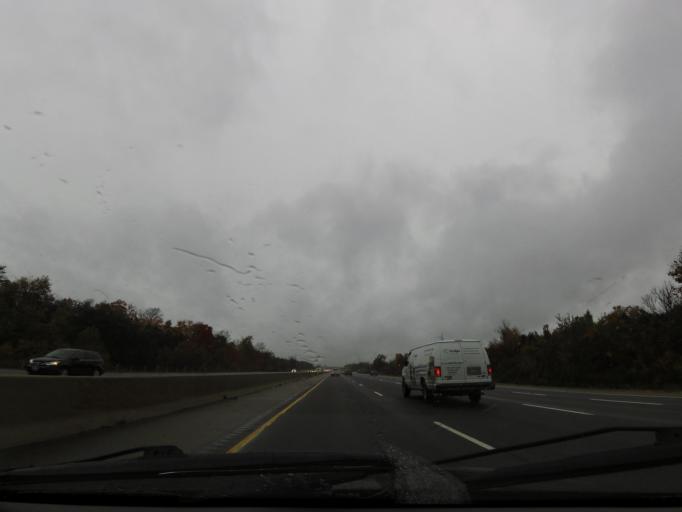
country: CA
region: Ontario
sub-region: Wellington County
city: Guelph
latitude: 43.4460
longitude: -80.1861
